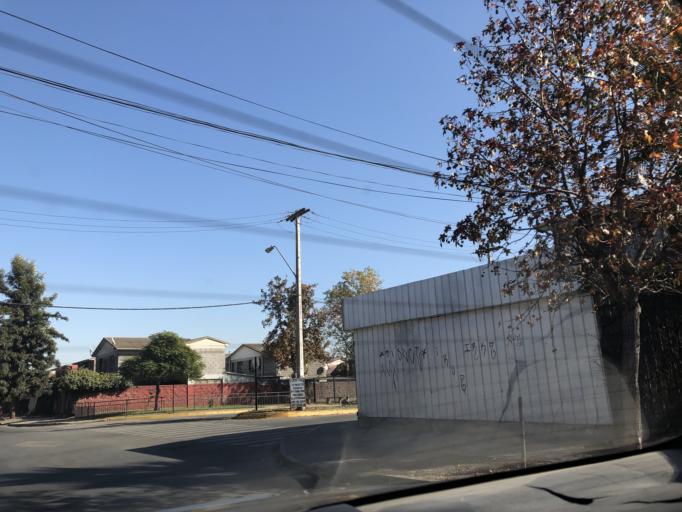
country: CL
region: Santiago Metropolitan
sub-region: Provincia de Santiago
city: La Pintana
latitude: -33.5762
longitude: -70.6020
